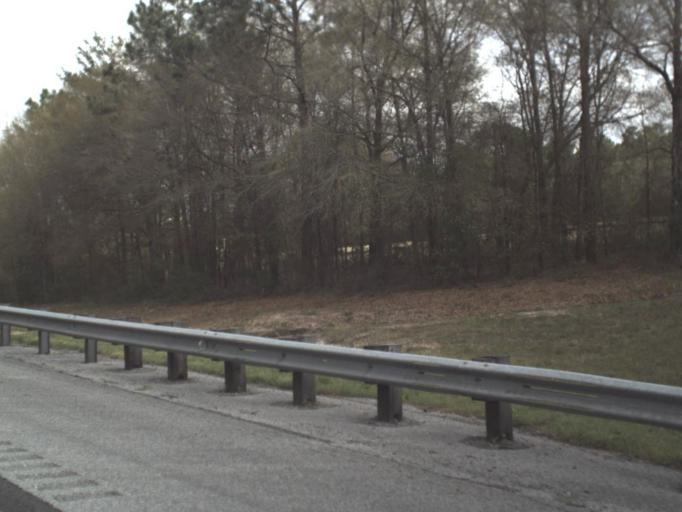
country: US
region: Florida
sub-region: Okaloosa County
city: Crestview
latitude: 30.7308
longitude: -86.3832
